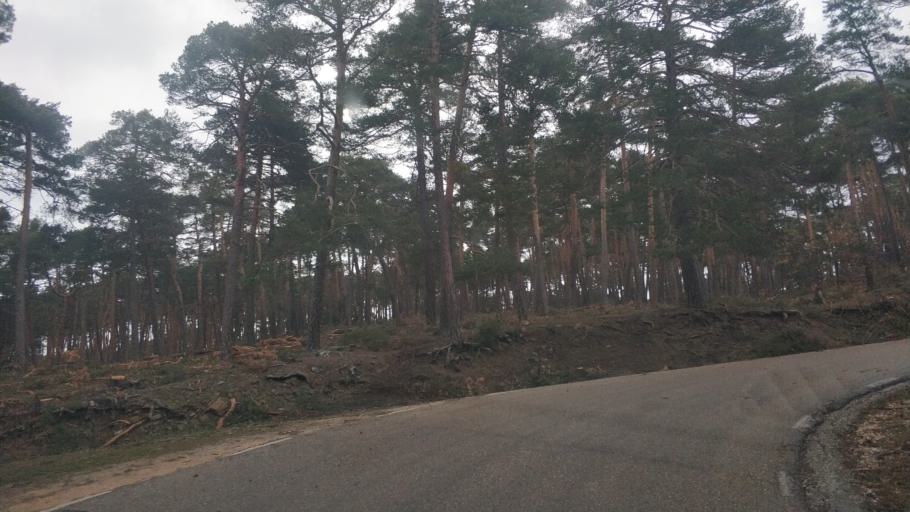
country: ES
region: Castille and Leon
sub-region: Provincia de Burgos
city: Canicosa de la Sierra
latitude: 41.9180
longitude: -3.0370
